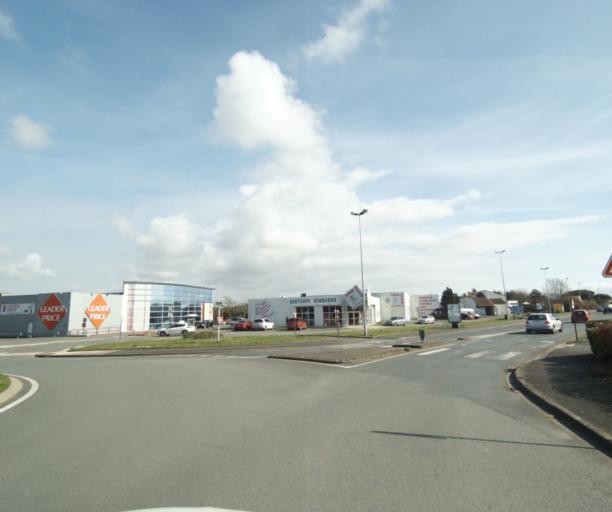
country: FR
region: Poitou-Charentes
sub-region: Departement de la Charente-Maritime
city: La Rochelle
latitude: 46.1739
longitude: -1.1666
